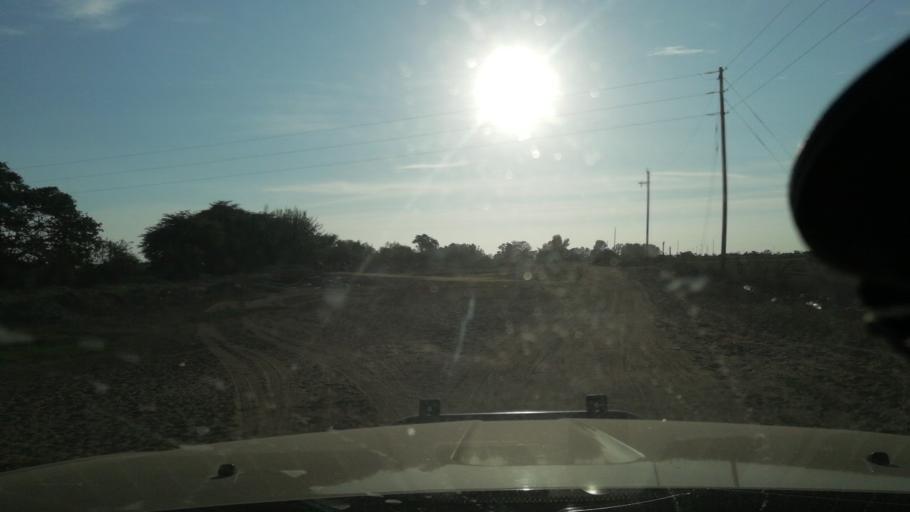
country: PE
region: Ica
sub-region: Provincia de Chincha
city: San Pedro
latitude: -13.3371
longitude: -76.1677
